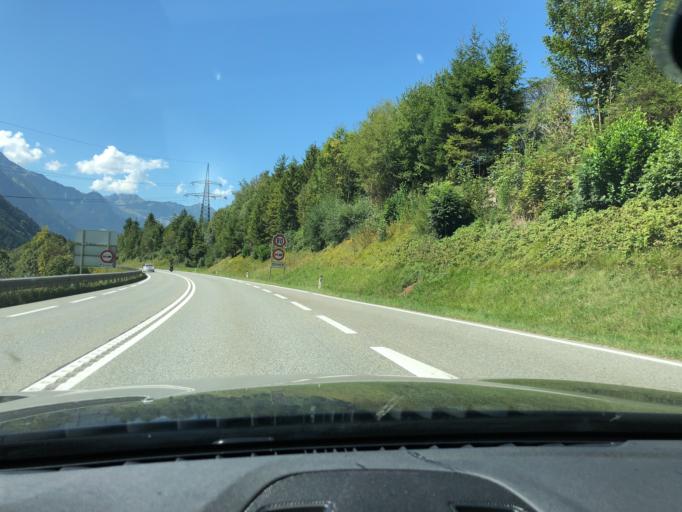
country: AT
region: Vorarlberg
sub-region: Politischer Bezirk Bludenz
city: Innerbraz
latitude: 47.1460
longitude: 9.8977
